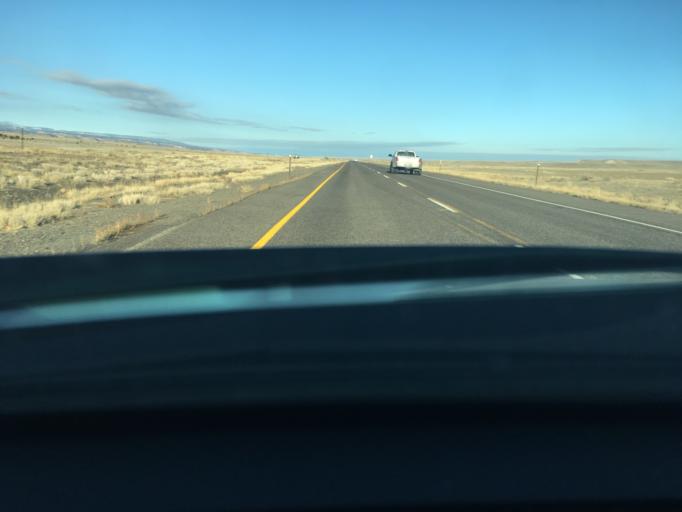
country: US
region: Colorado
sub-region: Delta County
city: Delta
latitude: 38.7885
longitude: -108.2519
